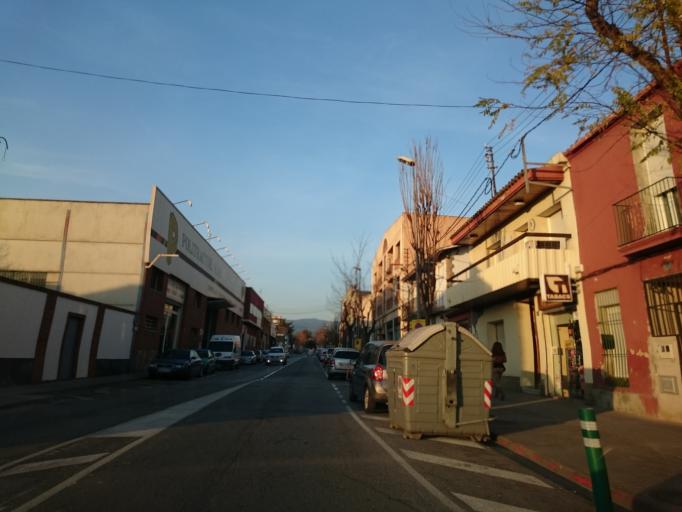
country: ES
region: Catalonia
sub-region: Provincia de Barcelona
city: Les Franqueses del Valles
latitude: 41.6305
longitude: 2.2956
